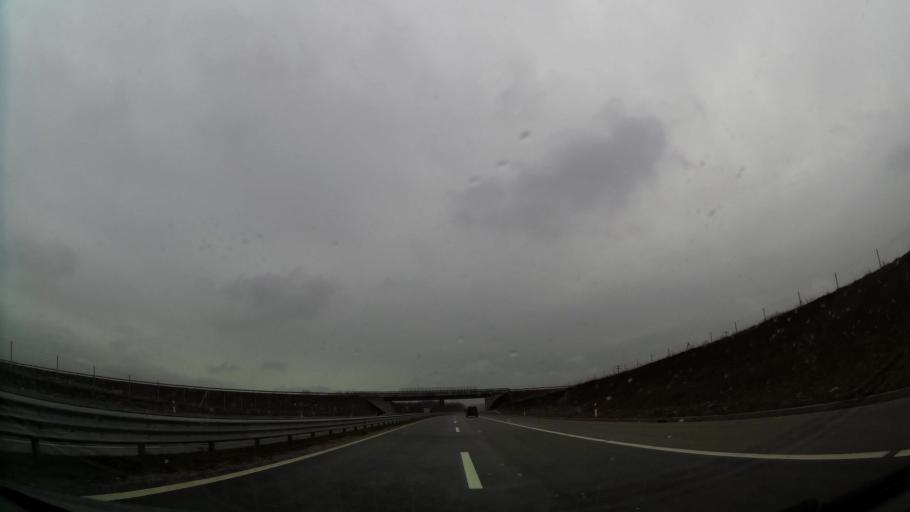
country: XK
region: Ferizaj
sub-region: Komuna e Ferizajt
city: Ferizaj
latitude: 42.3510
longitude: 21.2046
